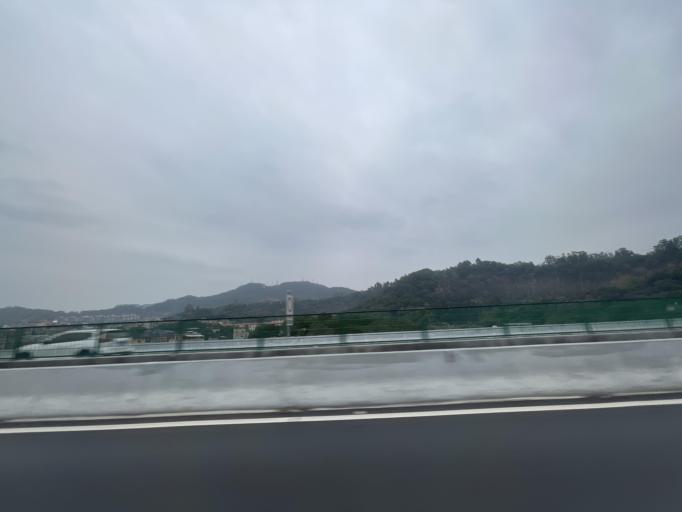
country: CN
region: Guangdong
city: Nansha
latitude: 22.7675
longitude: 113.5559
